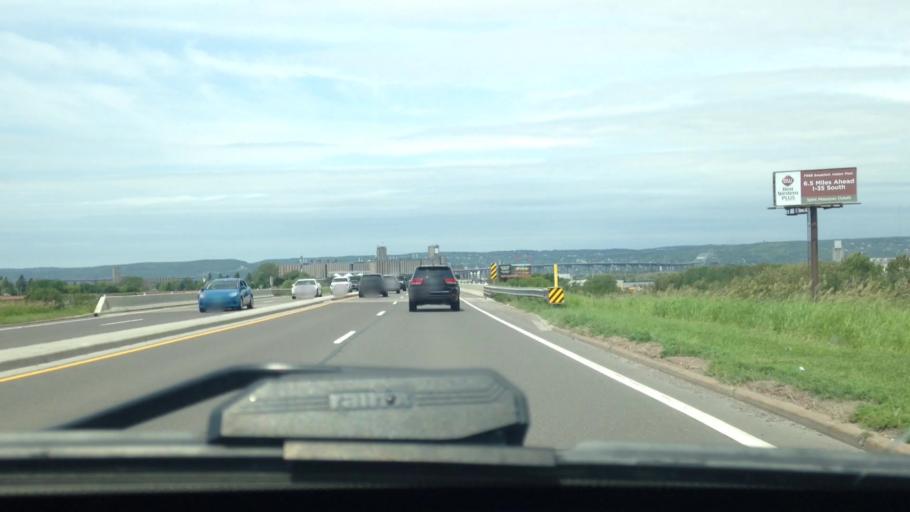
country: US
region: Wisconsin
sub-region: Douglas County
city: Superior
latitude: 46.7299
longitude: -92.0801
